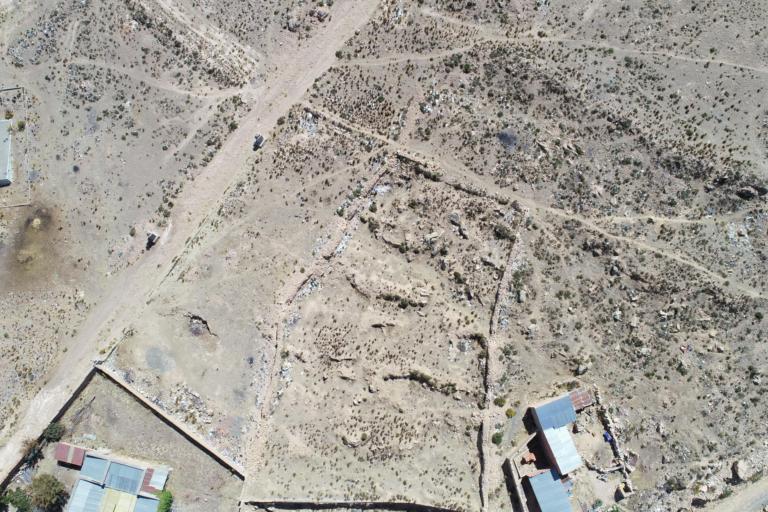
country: BO
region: La Paz
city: Achacachi
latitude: -16.0437
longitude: -68.6809
